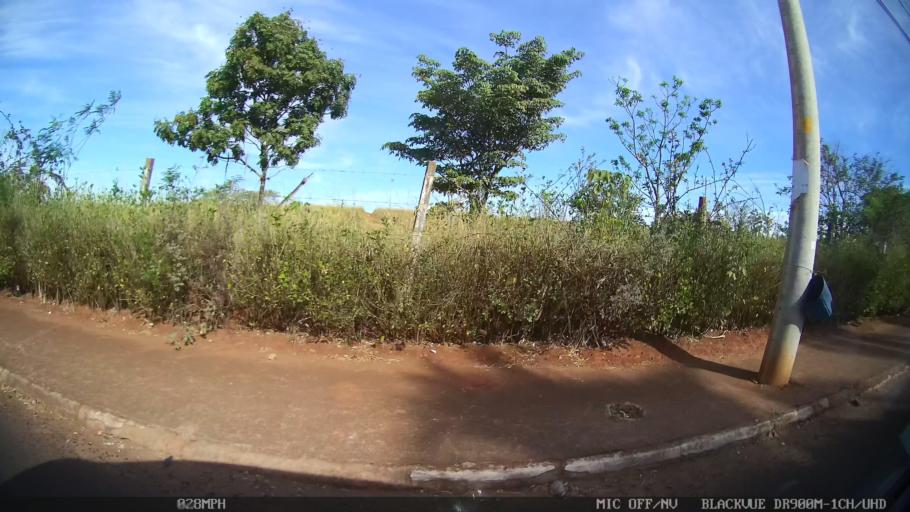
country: BR
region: Sao Paulo
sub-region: Sao Jose Do Rio Preto
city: Sao Jose do Rio Preto
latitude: -20.7980
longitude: -49.3285
